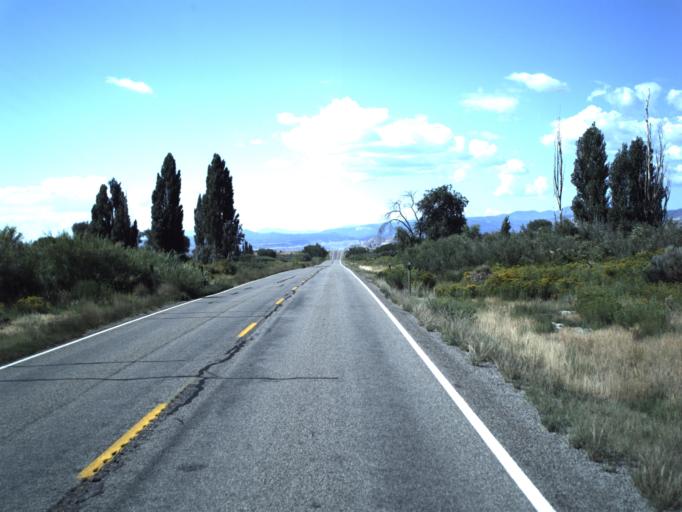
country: US
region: Utah
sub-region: Emery County
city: Ferron
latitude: 38.9068
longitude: -111.2705
